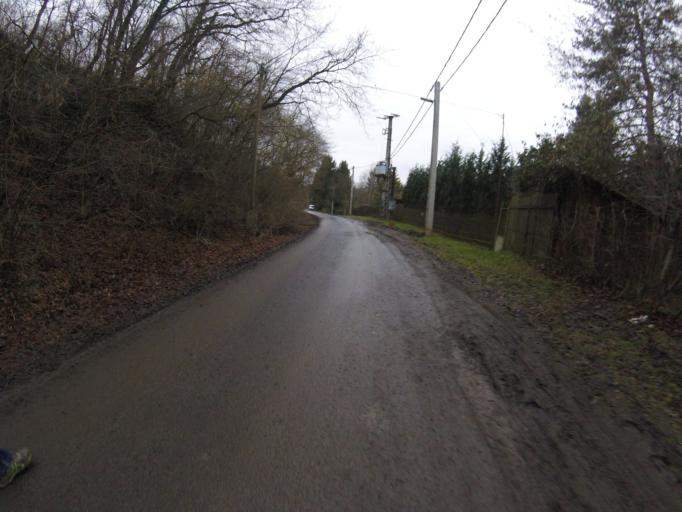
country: HU
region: Pest
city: Veroce
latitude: 47.8475
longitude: 19.0509
